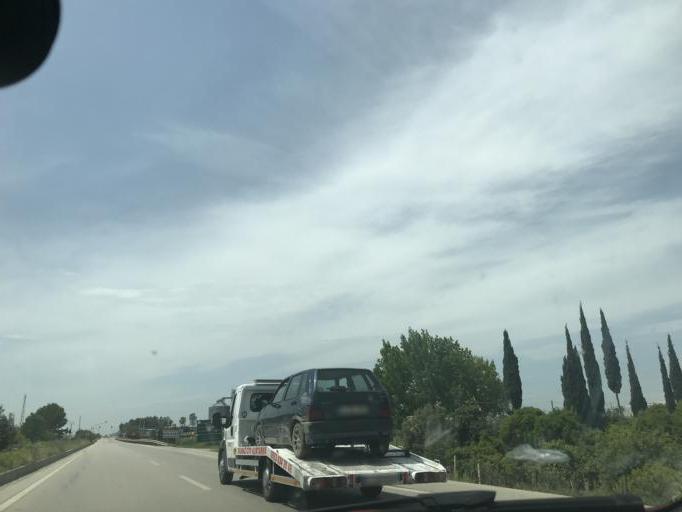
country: TR
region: Adana
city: Yakapinar
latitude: 36.9724
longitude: 35.5135
